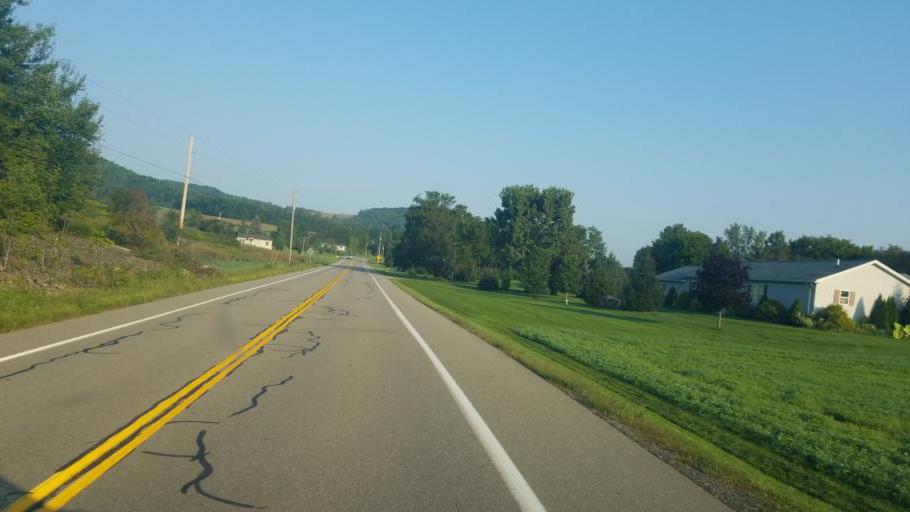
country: US
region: Pennsylvania
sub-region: Tioga County
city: Westfield
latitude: 42.0075
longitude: -77.5128
